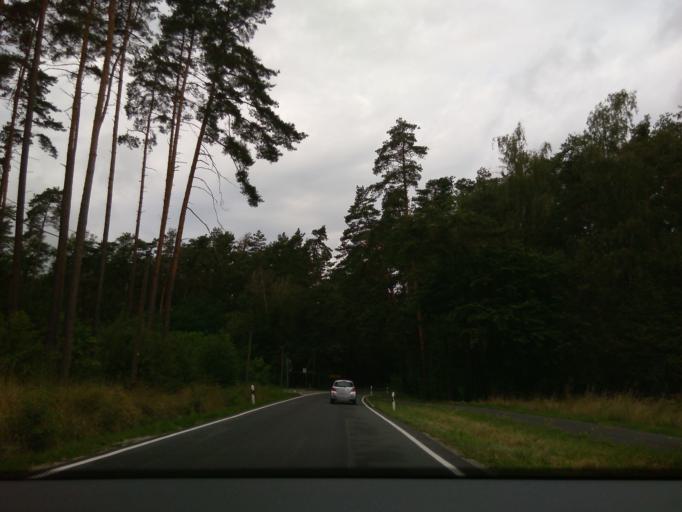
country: DE
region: Bavaria
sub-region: Regierungsbezirk Mittelfranken
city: Weisendorf
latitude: 49.6511
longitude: 10.8125
